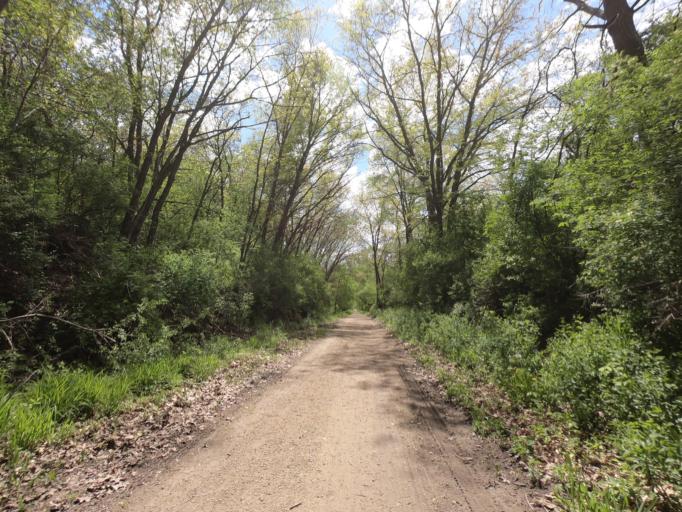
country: US
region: Wisconsin
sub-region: Dane County
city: Fitchburg
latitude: 42.9323
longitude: -89.5018
